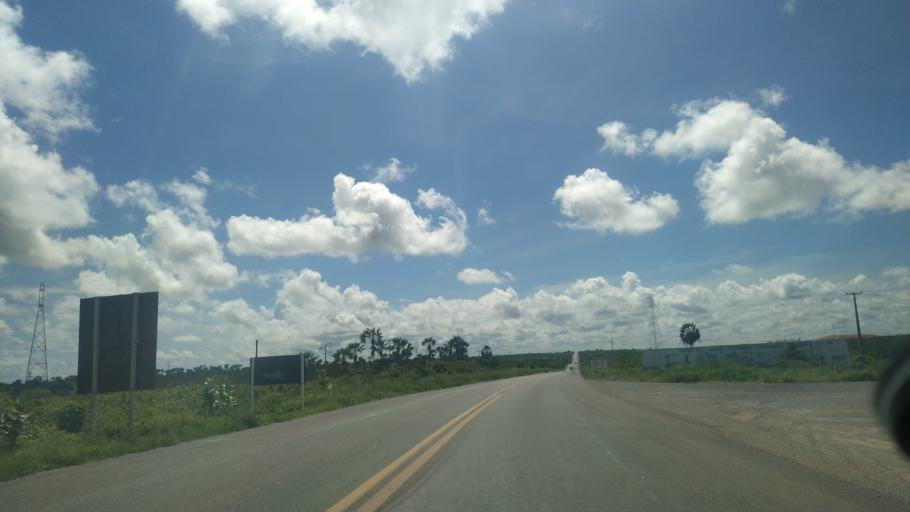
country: BR
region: Rio Grande do Norte
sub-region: Mossoro
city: Mossoro
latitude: -5.1828
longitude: -37.2977
